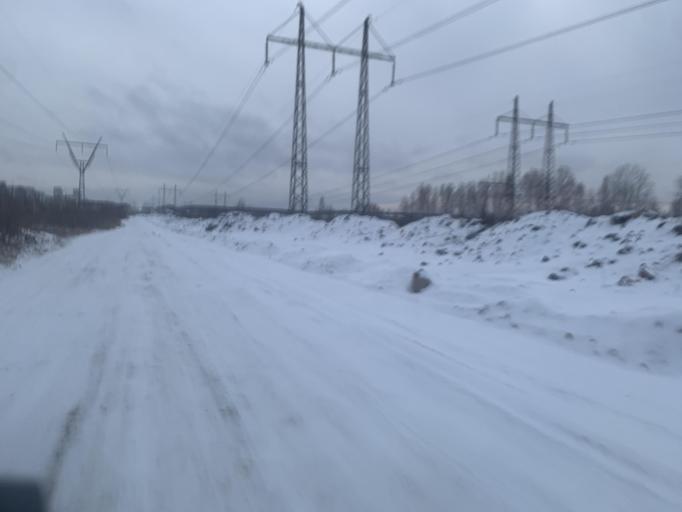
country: RU
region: Chelyabinsk
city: Roshchino
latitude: 55.1895
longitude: 61.2586
